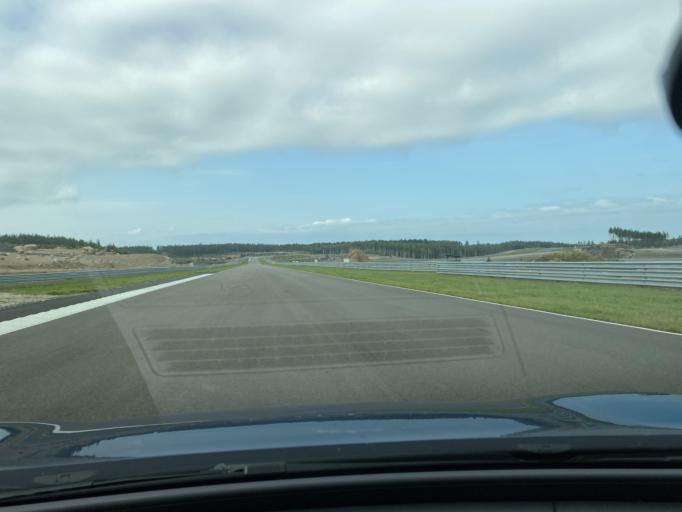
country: FI
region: Kymenlaakso
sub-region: Kouvola
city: Iitti
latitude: 60.8770
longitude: 26.4845
